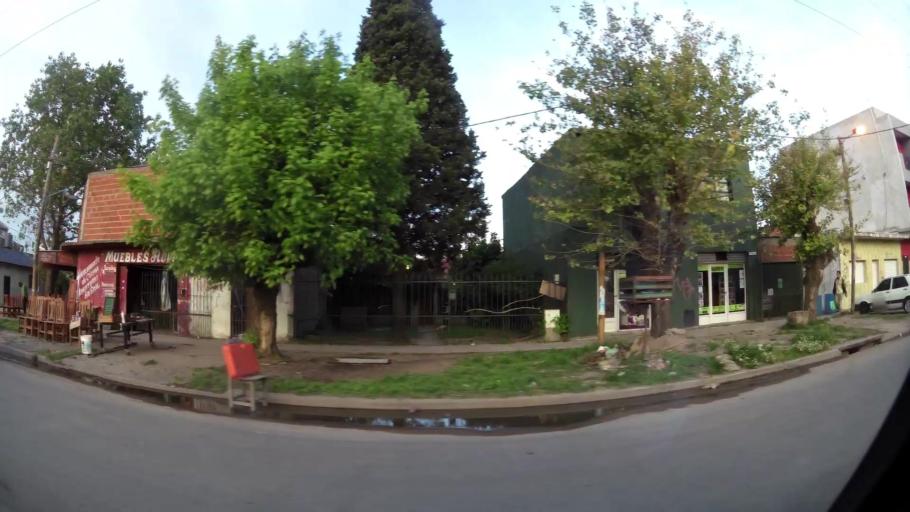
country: AR
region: Buenos Aires
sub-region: Partido de Almirante Brown
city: Adrogue
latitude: -34.7942
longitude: -58.3092
